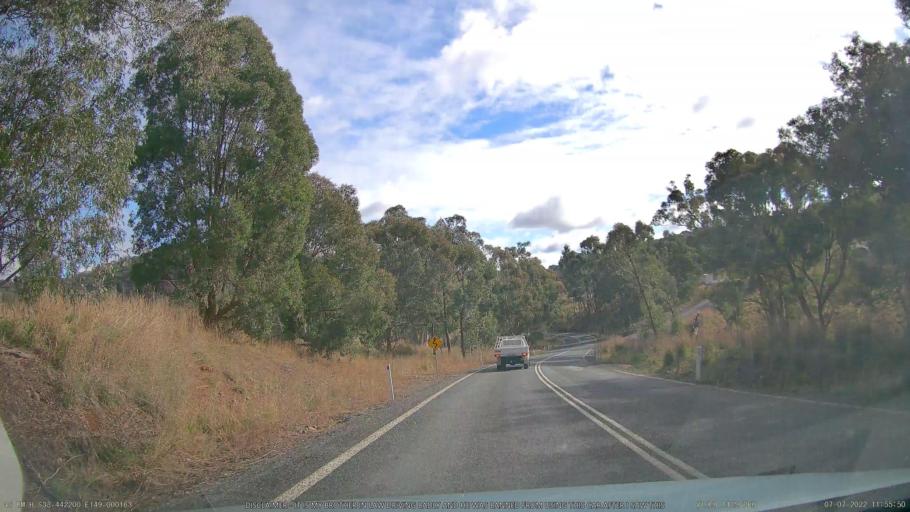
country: AU
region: New South Wales
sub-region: Blayney
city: Millthorpe
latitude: -33.4420
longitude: 148.9999
